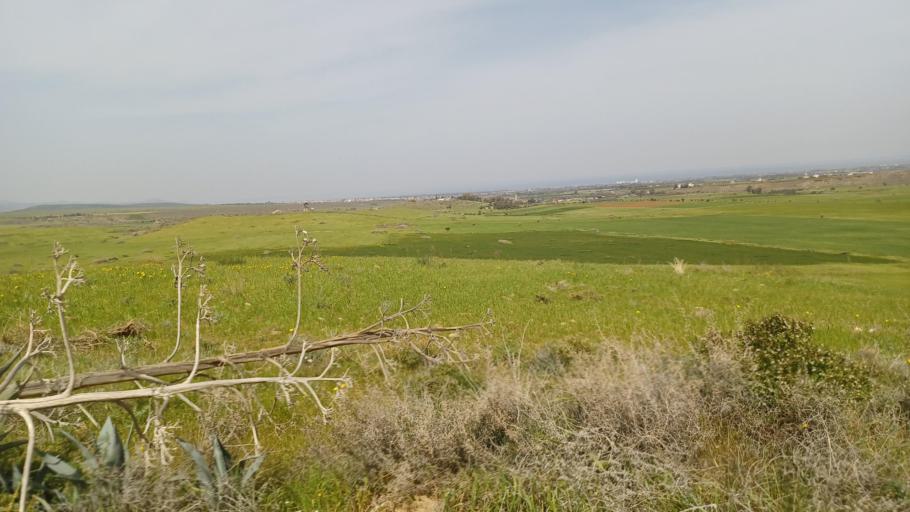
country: CY
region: Lefkosia
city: Astromeritis
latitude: 35.1069
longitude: 32.9620
